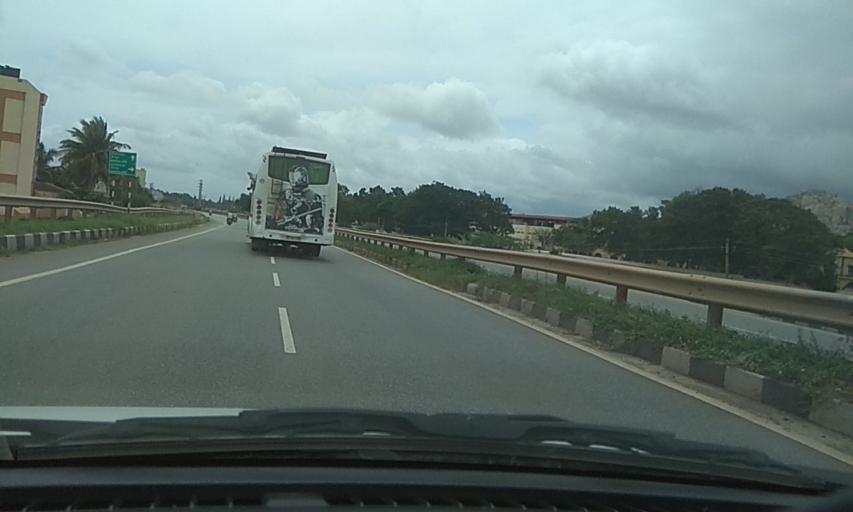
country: IN
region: Karnataka
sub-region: Chitradurga
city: Chitradurga
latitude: 14.2394
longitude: 76.3759
